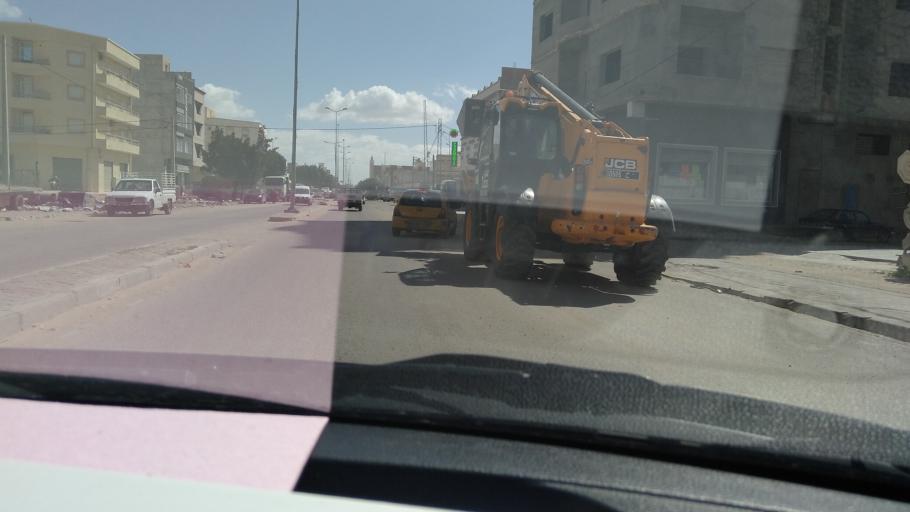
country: TN
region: Al Qayrawan
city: Kairouan
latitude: 35.6830
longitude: 10.0769
